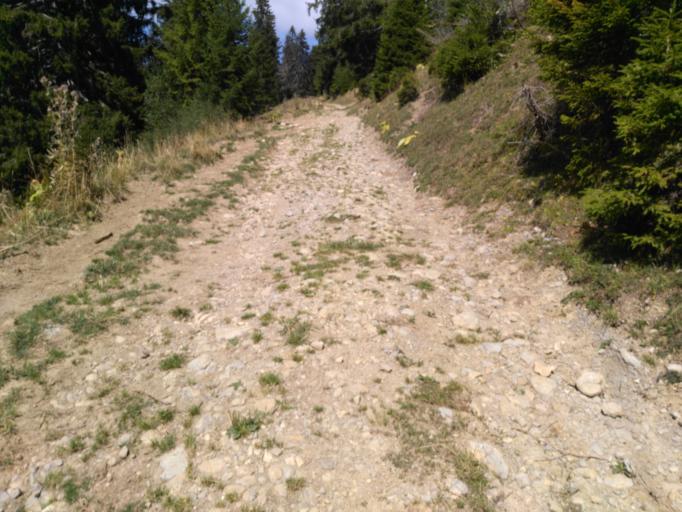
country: FR
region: Rhone-Alpes
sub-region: Departement de la Haute-Savoie
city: Viuz-la-Chiesaz
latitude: 45.7865
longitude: 6.1062
